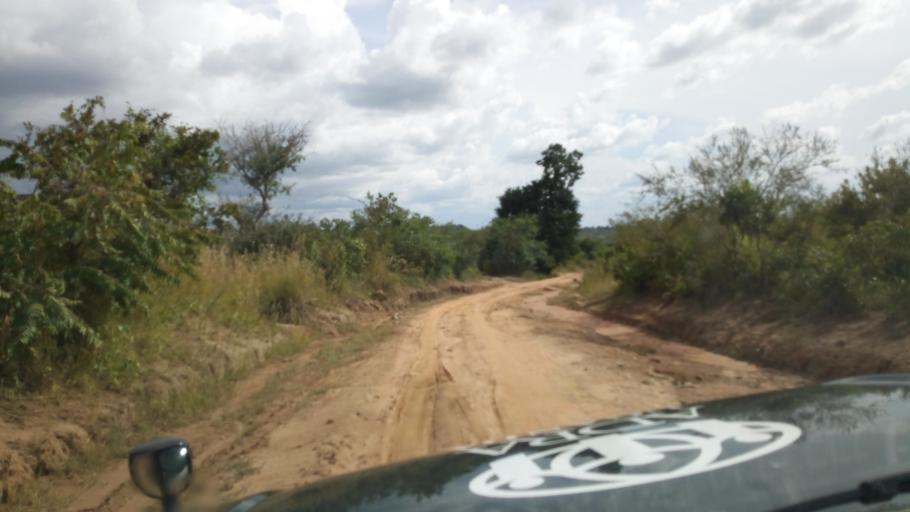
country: UG
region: Northern Region
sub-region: Adjumani District
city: Adjumani
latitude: 3.4279
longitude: 31.8856
